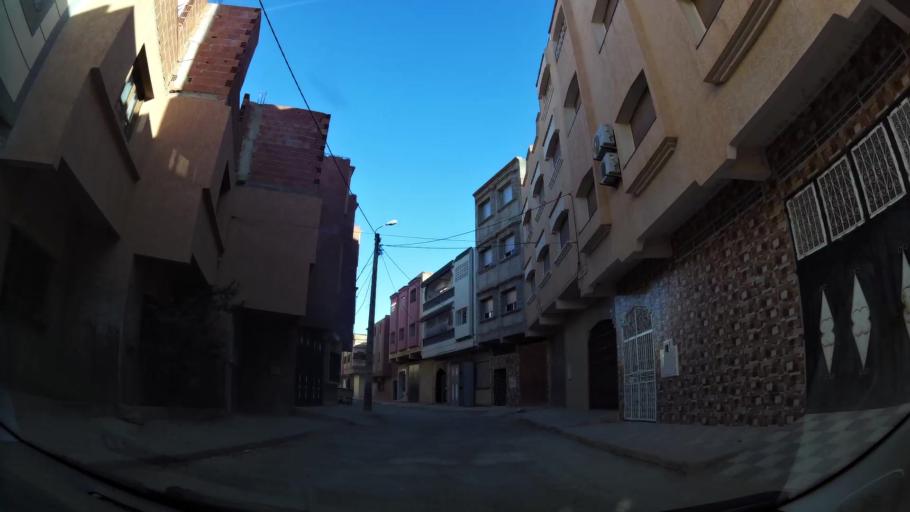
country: MA
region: Oriental
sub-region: Berkane-Taourirt
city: Berkane
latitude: 34.9272
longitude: -2.3396
